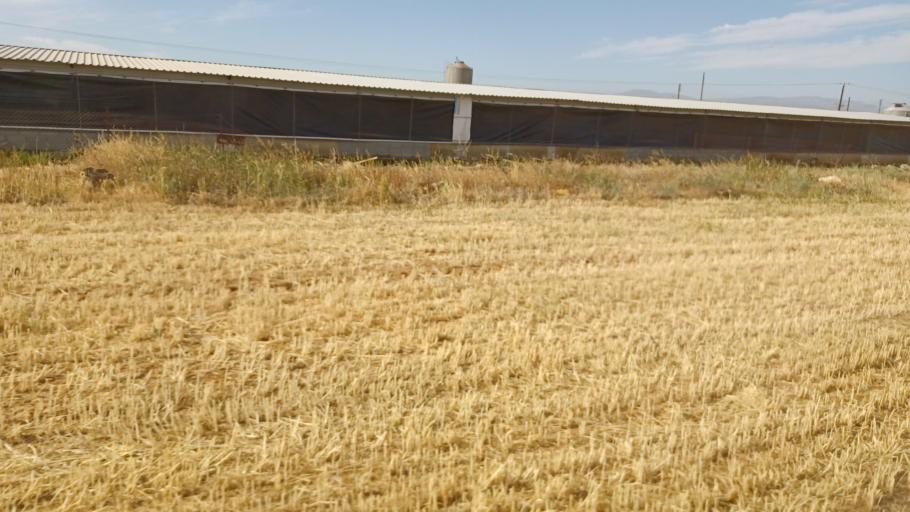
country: CY
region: Lefkosia
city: Kokkinotrimithia
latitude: 35.1629
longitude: 33.1933
